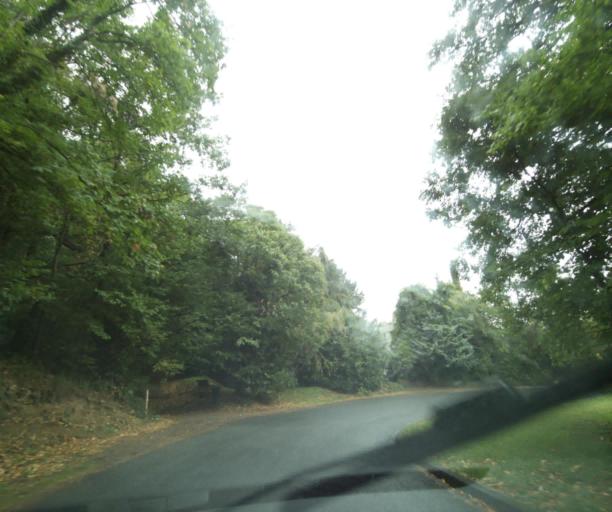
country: FR
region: Auvergne
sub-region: Departement du Puy-de-Dome
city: Ceyrat
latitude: 45.7304
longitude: 3.0607
